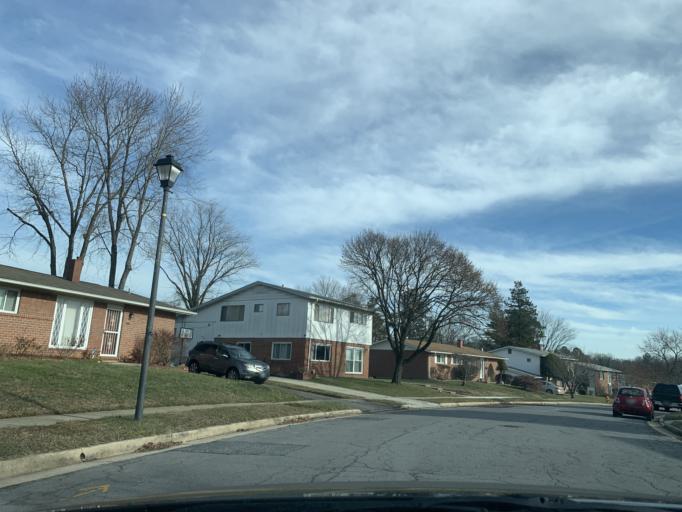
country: US
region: Maryland
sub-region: Baltimore County
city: Pikesville
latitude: 39.3692
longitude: -76.7438
